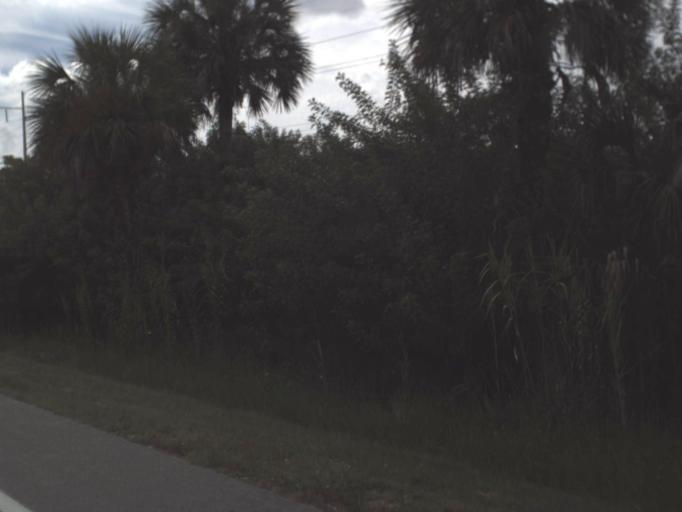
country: US
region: Florida
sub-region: Collier County
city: Marco
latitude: 25.9223
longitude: -81.3581
